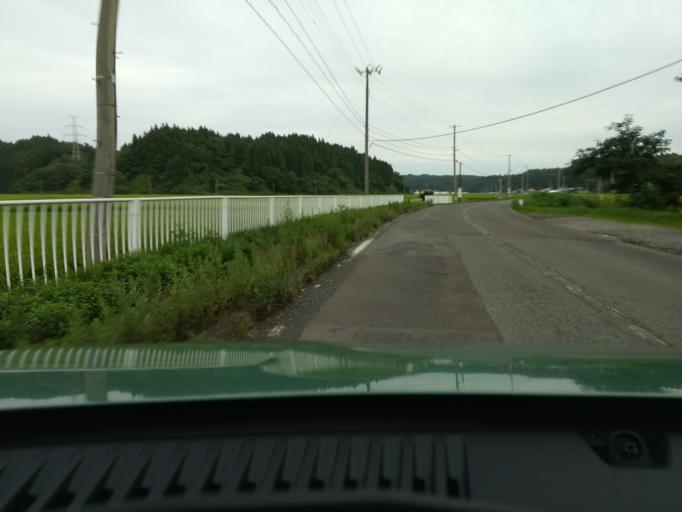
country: JP
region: Akita
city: Akita
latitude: 39.7886
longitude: 140.1199
